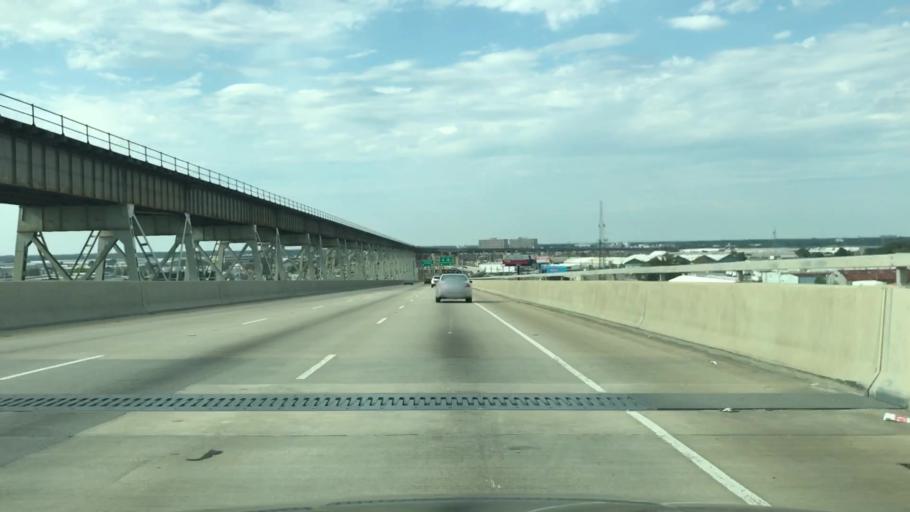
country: US
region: Louisiana
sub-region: Jefferson Parish
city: Bridge City
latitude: 29.9485
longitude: -90.1735
